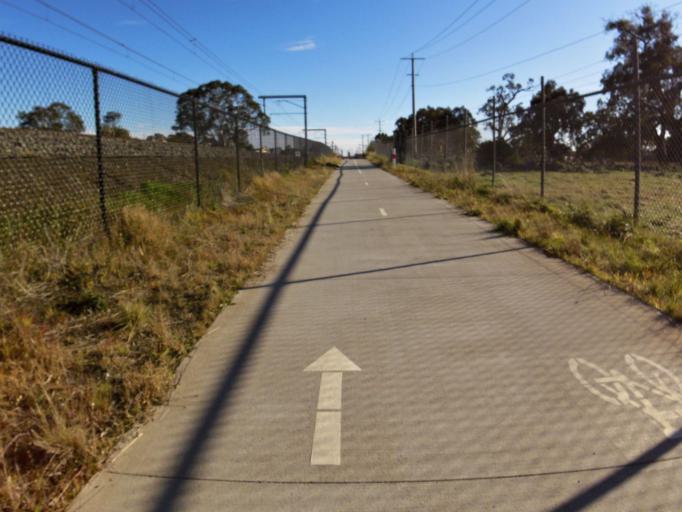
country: AU
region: Victoria
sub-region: Whittlesea
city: Mill Park
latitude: -37.6475
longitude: 145.0797
